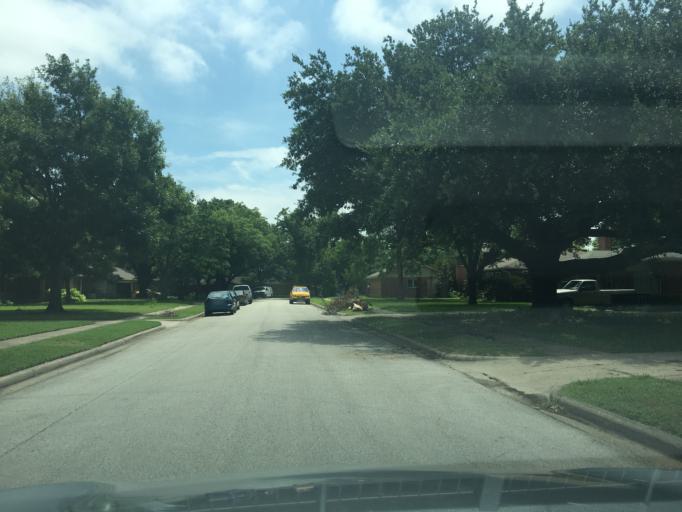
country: US
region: Texas
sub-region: Dallas County
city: Richardson
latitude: 32.9462
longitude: -96.7422
